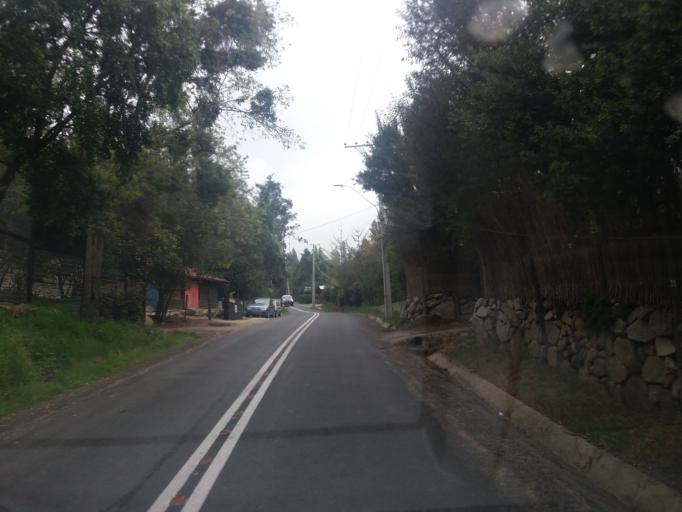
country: CL
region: Valparaiso
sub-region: Provincia de Marga Marga
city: Limache
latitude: -33.0226
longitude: -71.0723
